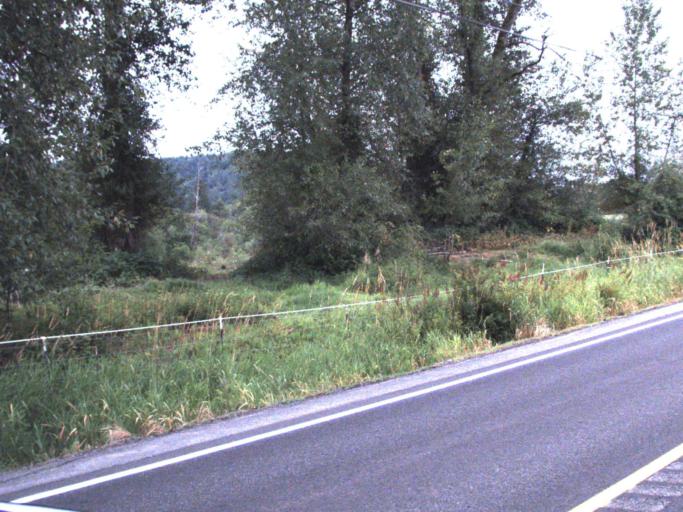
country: US
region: Washington
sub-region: King County
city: Carnation
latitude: 47.6115
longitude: -121.9113
